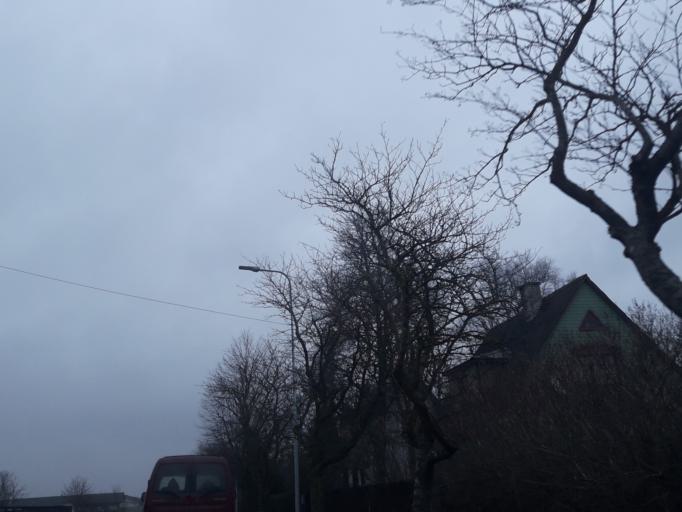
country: EE
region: Saare
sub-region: Kuressaare linn
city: Kuressaare
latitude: 58.2550
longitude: 22.4775
